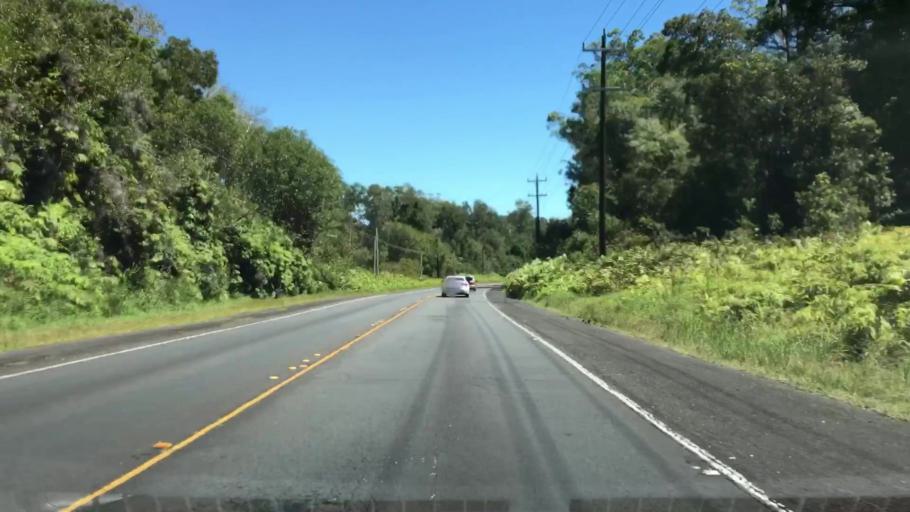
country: US
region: Hawaii
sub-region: Hawaii County
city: Volcano
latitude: 19.4698
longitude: -155.1645
